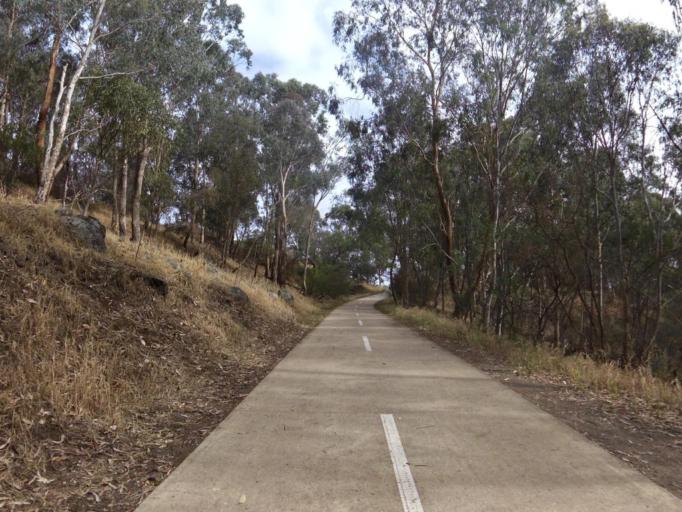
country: AU
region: Victoria
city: Alphington
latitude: -37.7753
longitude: 145.0348
